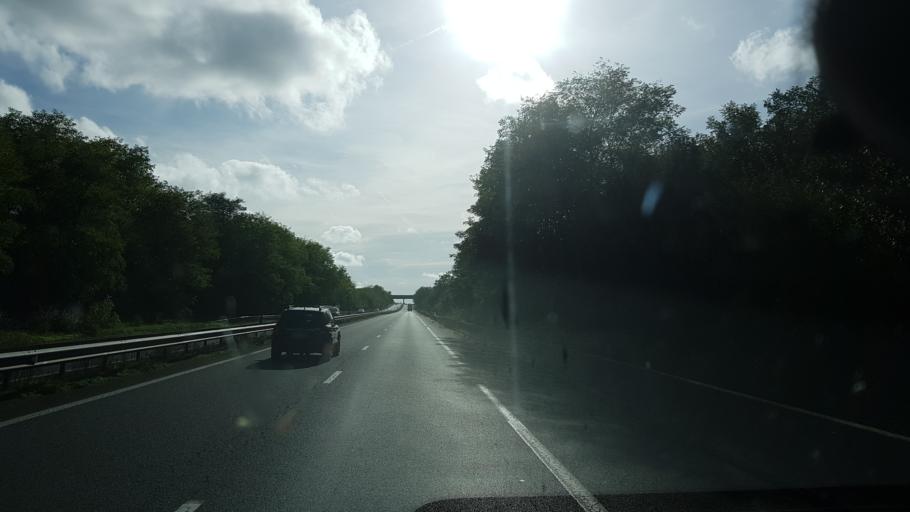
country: FR
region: Poitou-Charentes
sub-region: Departement de la Charente
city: Taponnat-Fleurignac
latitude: 45.7761
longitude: 0.4040
